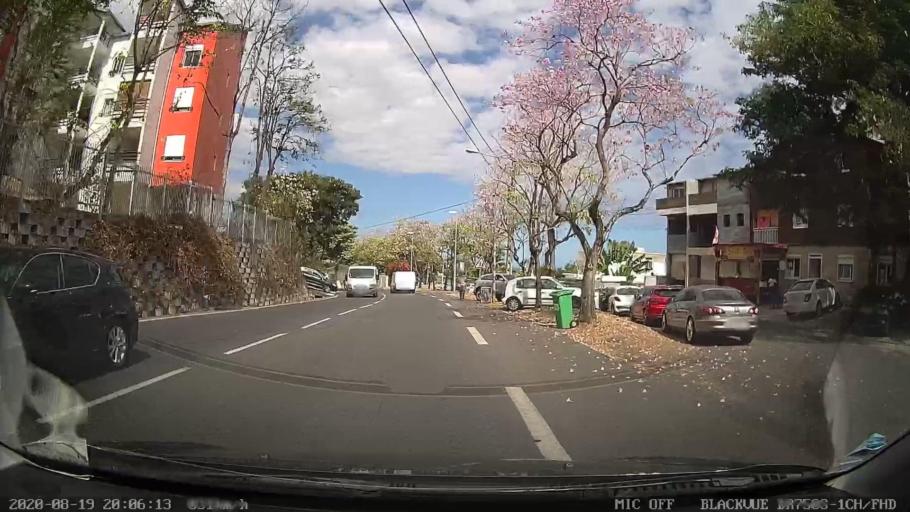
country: RE
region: Reunion
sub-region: Reunion
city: La Possession
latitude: -20.9564
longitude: 55.3369
